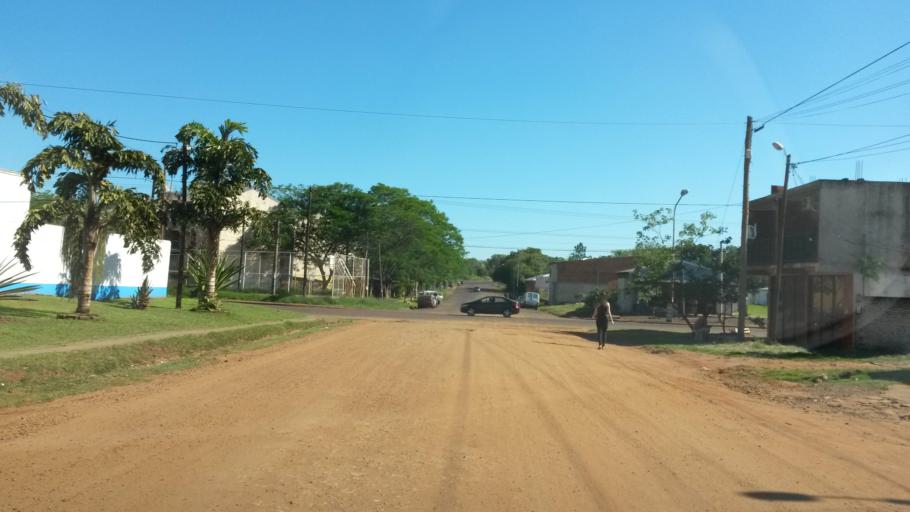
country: AR
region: Misiones
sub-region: Departamento de Capital
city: Posadas
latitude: -27.3697
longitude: -55.9359
